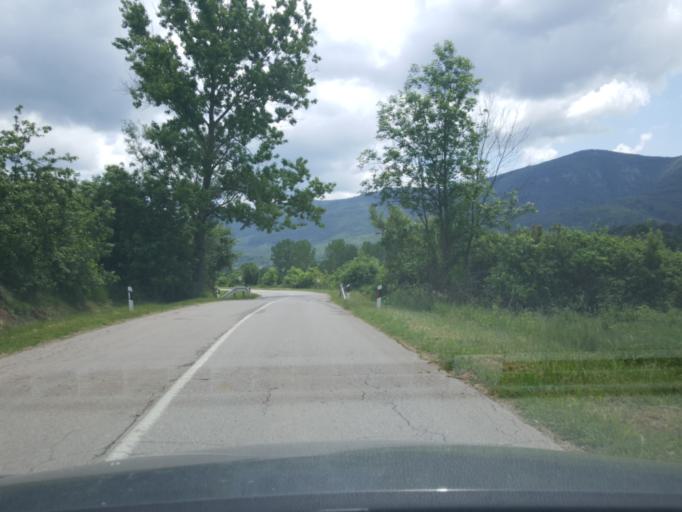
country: RS
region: Central Serbia
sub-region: Zajecarski Okrug
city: Soko Banja
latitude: 43.6456
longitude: 21.9335
